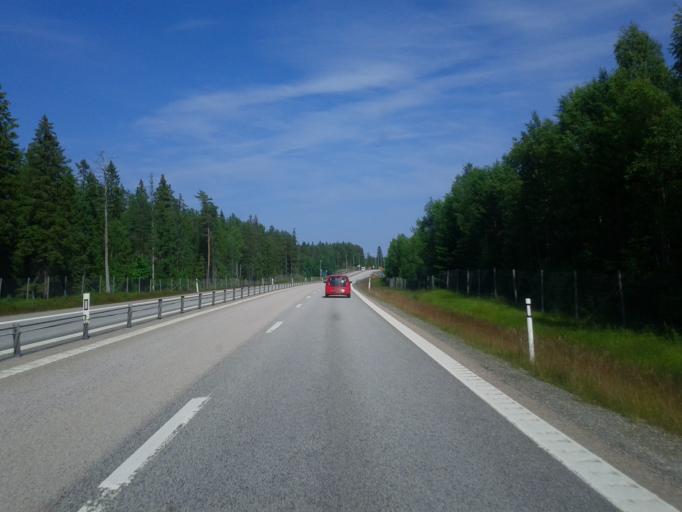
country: SE
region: Vaesterbotten
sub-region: Umea Kommun
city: Hoernefors
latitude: 63.6255
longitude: 19.8536
